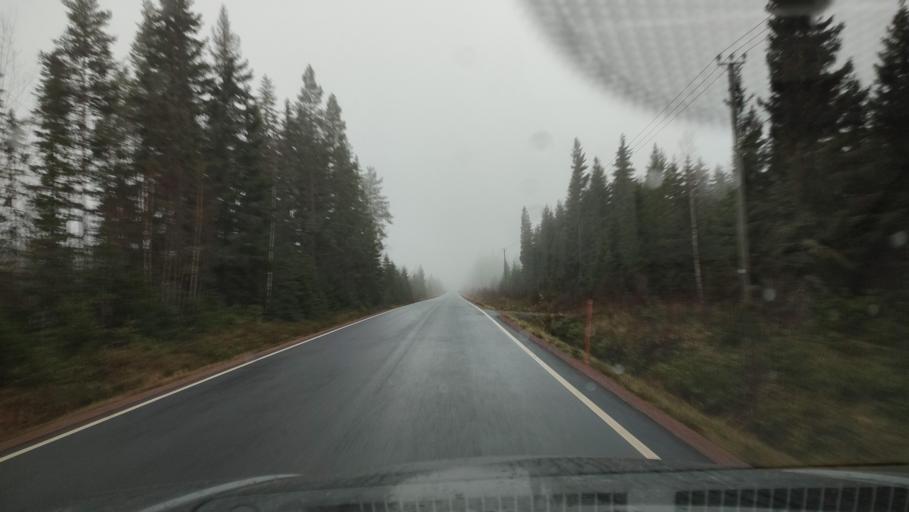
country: FI
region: Southern Ostrobothnia
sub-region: Suupohja
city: Karijoki
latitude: 62.1755
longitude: 21.7629
